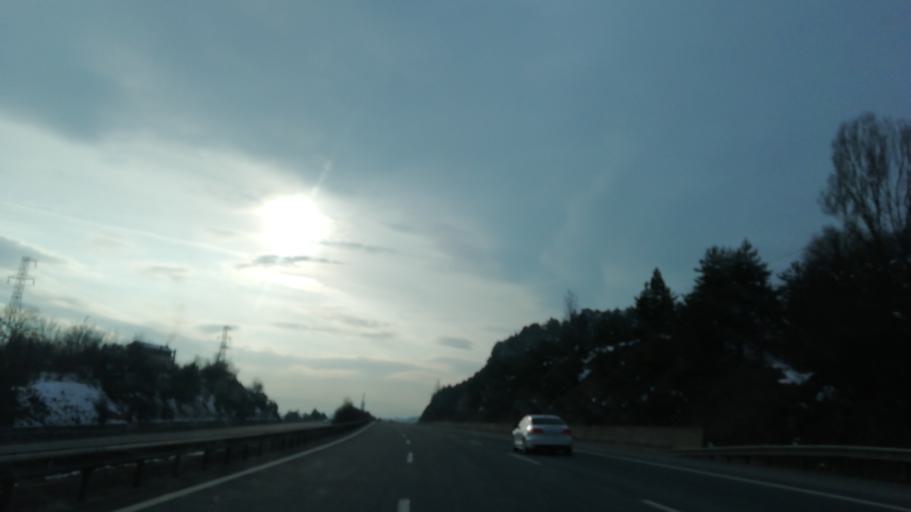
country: TR
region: Bolu
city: Bolu
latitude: 40.7601
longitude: 31.5855
